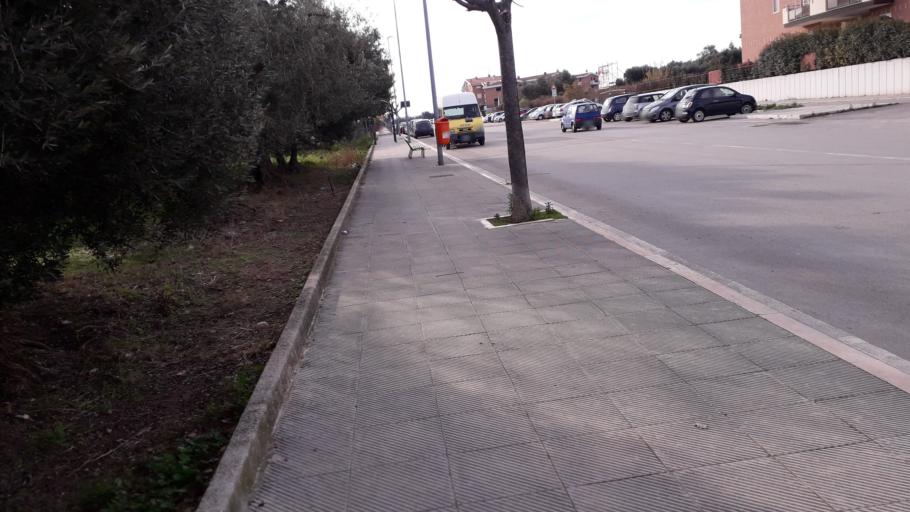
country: IT
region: Molise
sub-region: Provincia di Campobasso
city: Campomarino
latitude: 41.9532
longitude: 15.0319
